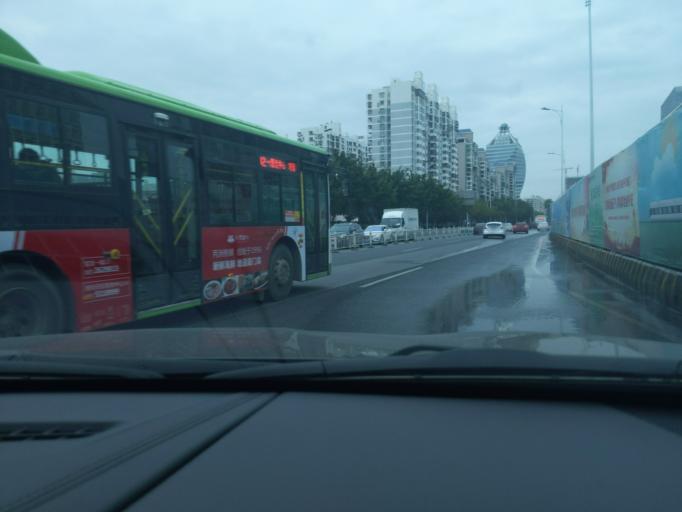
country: CN
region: Fujian
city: Liuwudian
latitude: 24.4833
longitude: 118.1810
